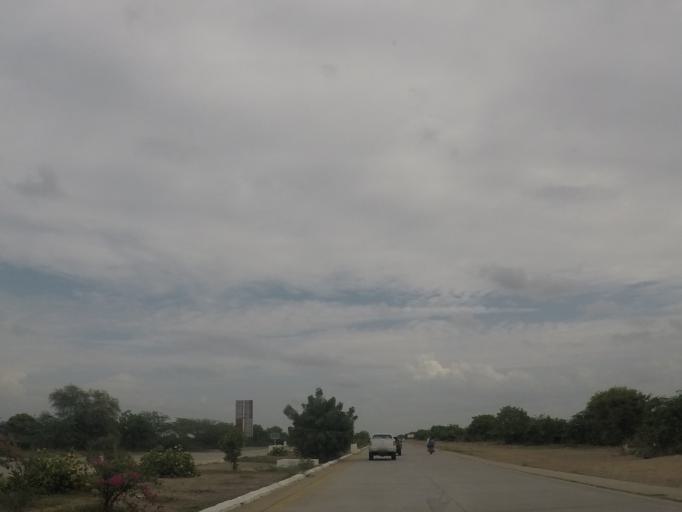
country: MM
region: Sagain
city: Sagaing
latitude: 21.7985
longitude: 95.9670
